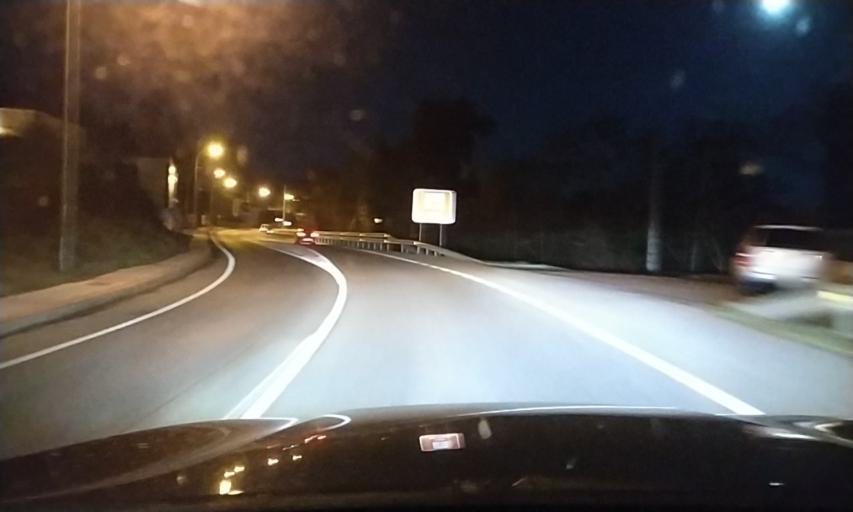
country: ES
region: Galicia
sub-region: Provincia de Ourense
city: Verin
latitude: 41.9383
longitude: -7.4483
